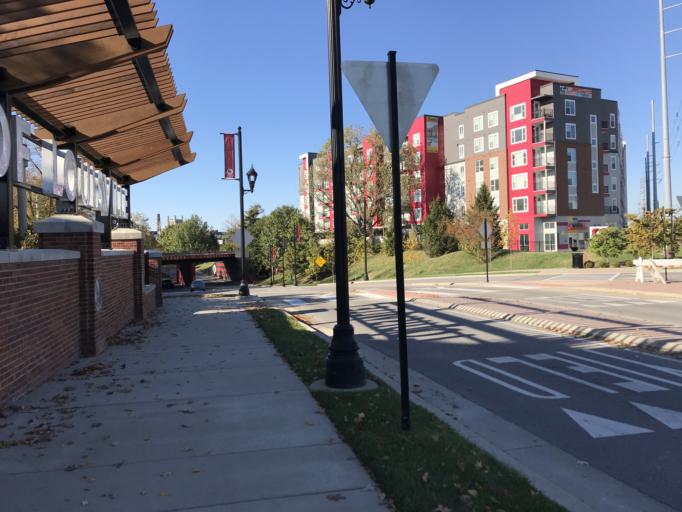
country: US
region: Kentucky
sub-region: Jefferson County
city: Audubon Park
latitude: 38.2184
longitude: -85.7546
